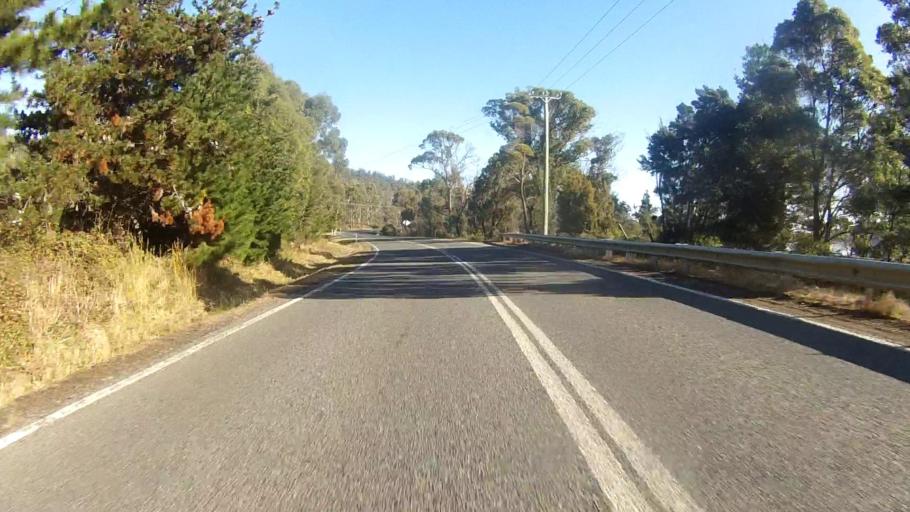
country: AU
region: Tasmania
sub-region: Clarence
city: Sandford
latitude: -43.0232
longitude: 147.8920
